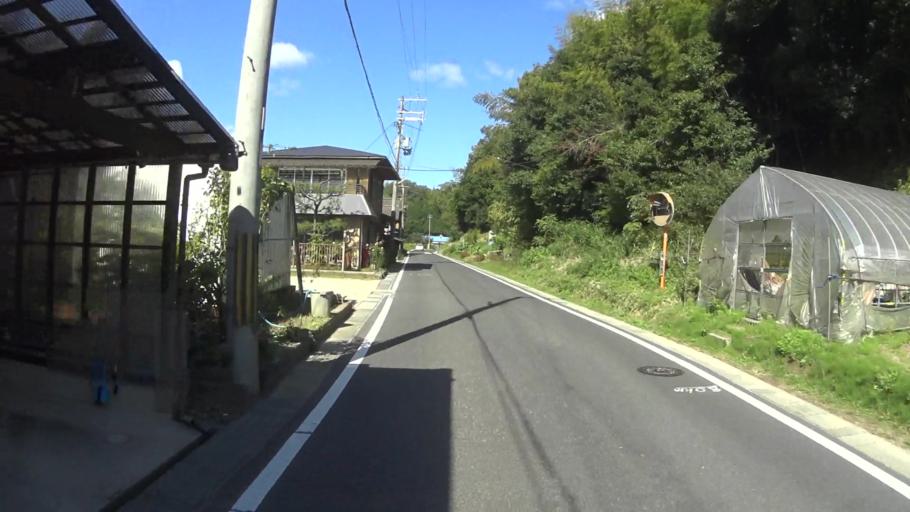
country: JP
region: Kyoto
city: Miyazu
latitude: 35.6341
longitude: 135.0718
